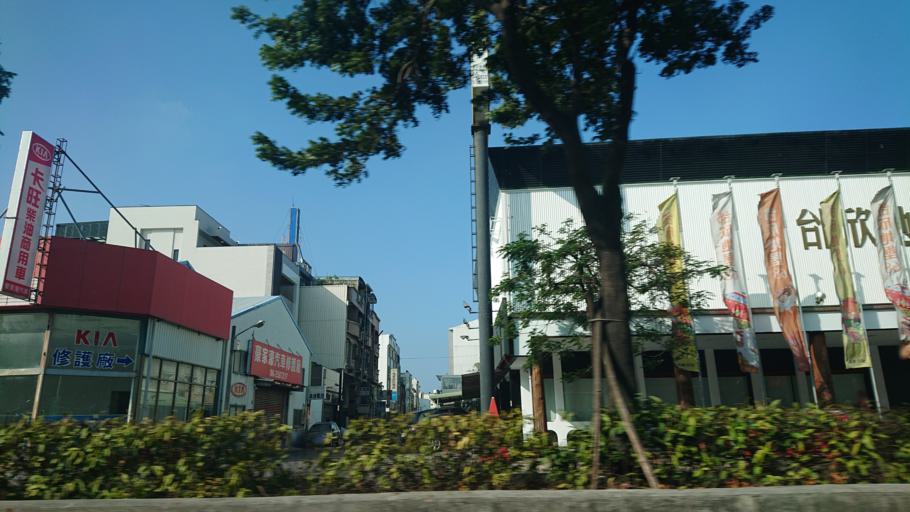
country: TW
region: Taiwan
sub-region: Tainan
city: Tainan
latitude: 23.0106
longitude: 120.1852
